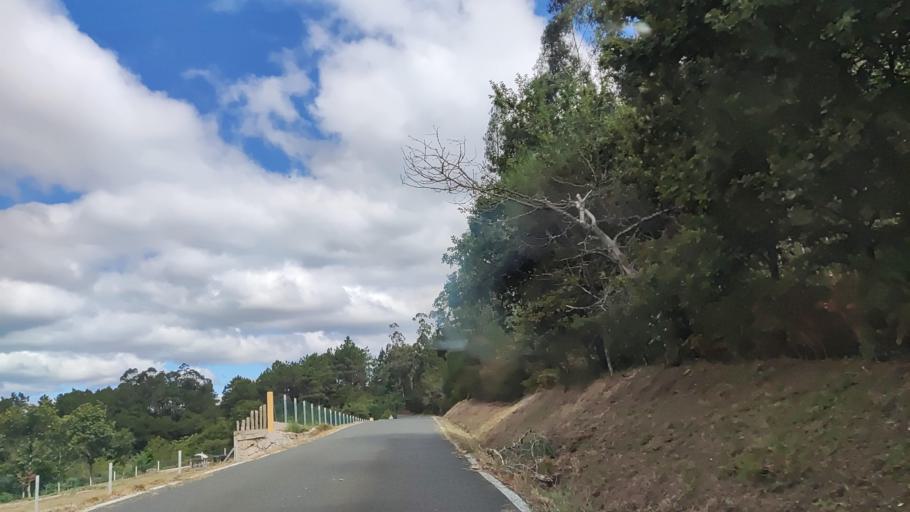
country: ES
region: Galicia
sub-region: Provincia da Coruna
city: Rois
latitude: 42.7488
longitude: -8.7017
